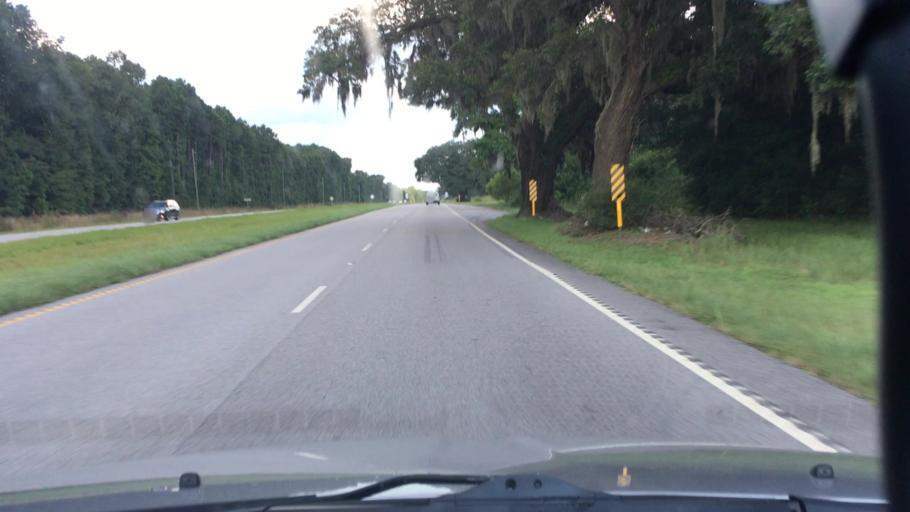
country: US
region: South Carolina
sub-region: Hampton County
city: Yemassee
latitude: 32.6394
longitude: -80.8487
